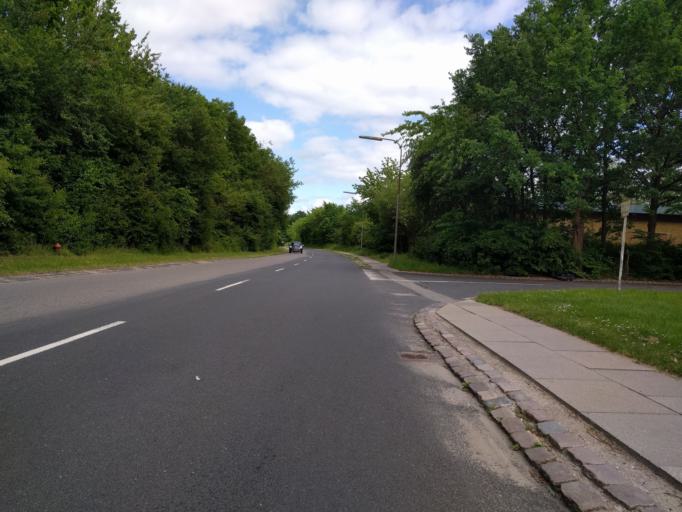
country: DK
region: South Denmark
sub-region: Odense Kommune
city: Seden
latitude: 55.4056
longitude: 10.4451
